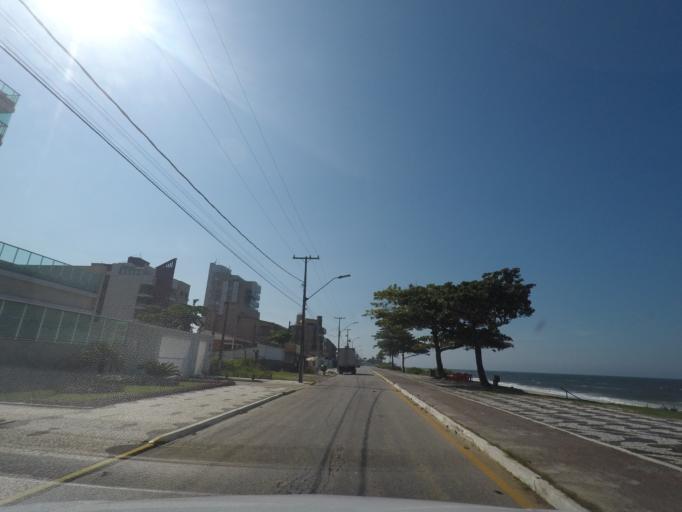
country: BR
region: Parana
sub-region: Guaratuba
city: Guaratuba
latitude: -25.8239
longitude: -48.5328
